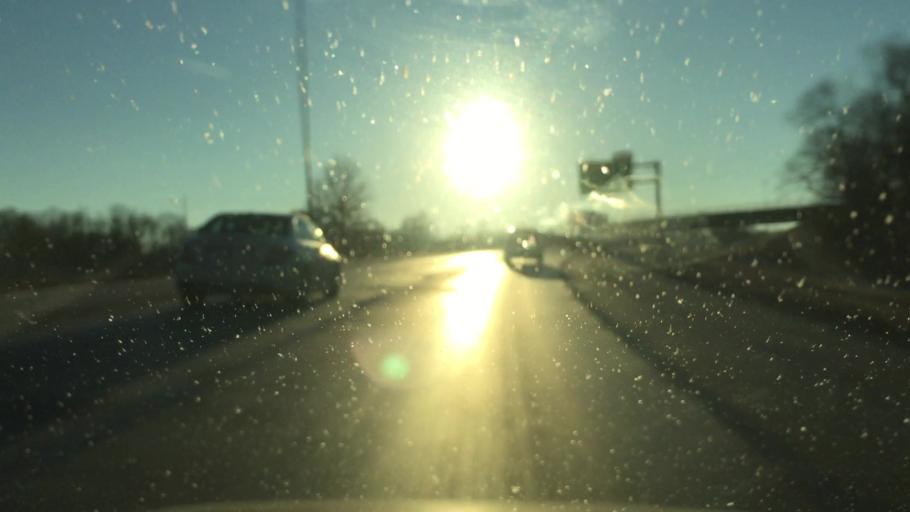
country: US
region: Kansas
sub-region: Wyandotte County
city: Kansas City
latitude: 39.1477
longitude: -94.6572
